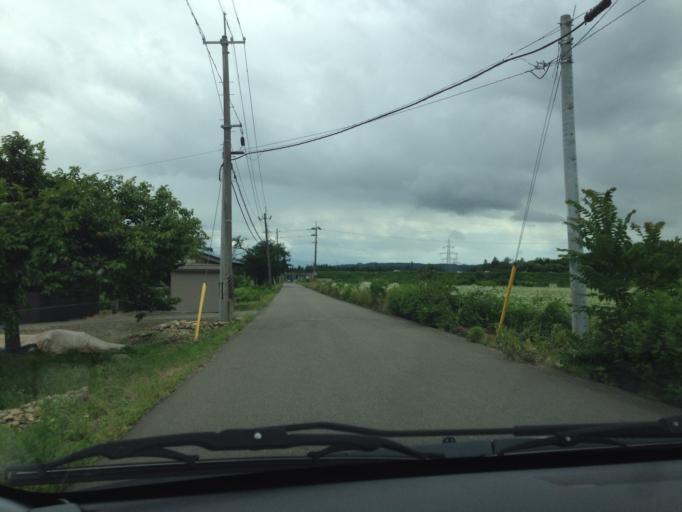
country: JP
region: Fukushima
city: Kitakata
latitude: 37.7072
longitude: 139.8726
